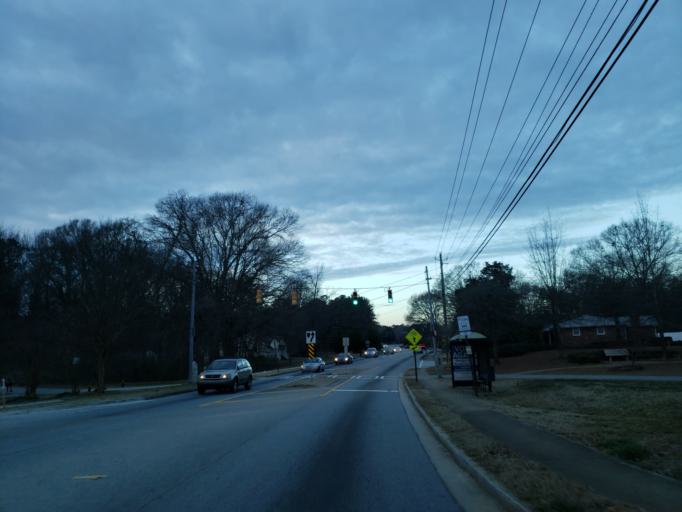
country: US
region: Georgia
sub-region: Cobb County
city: Mableton
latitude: 33.8470
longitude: -84.5851
